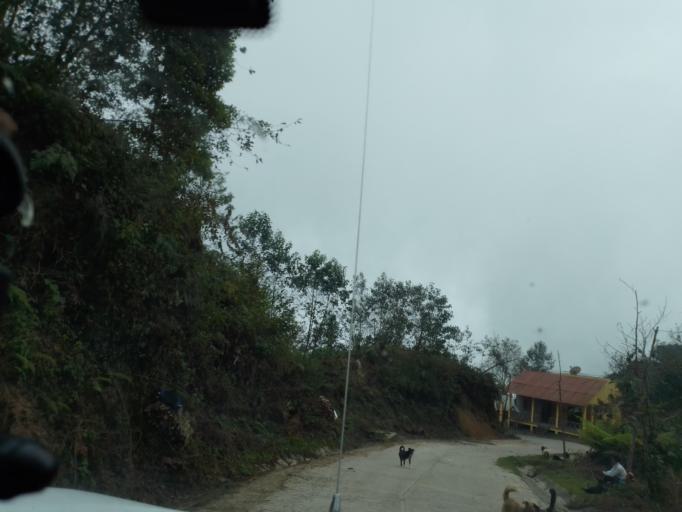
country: MX
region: Chiapas
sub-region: Union Juarez
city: Santo Domingo
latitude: 15.0928
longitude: -92.0999
